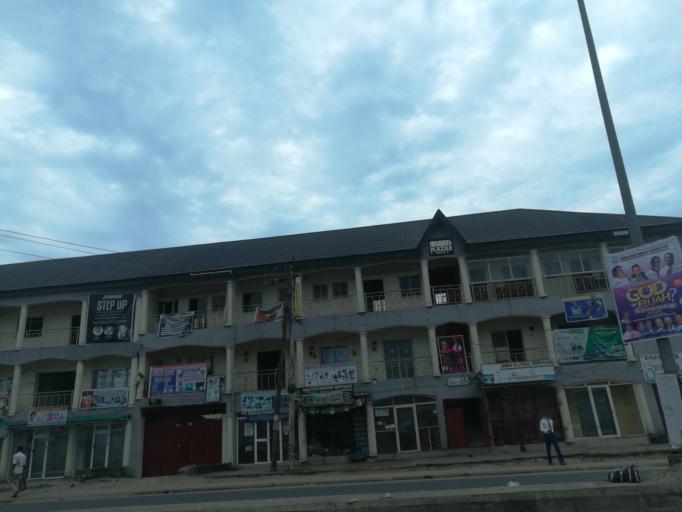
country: NG
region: Rivers
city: Port Harcourt
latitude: 4.8137
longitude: 6.9484
